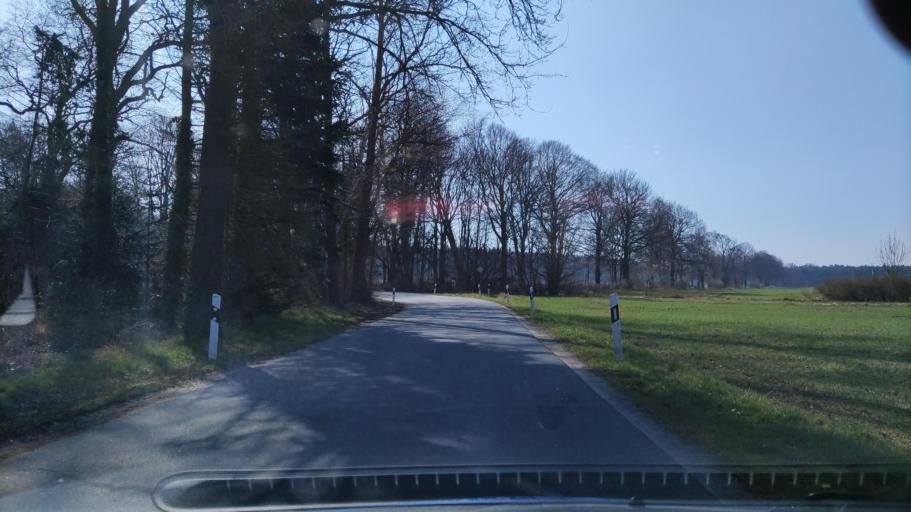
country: DE
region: Lower Saxony
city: Zernien
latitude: 52.9849
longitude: 10.8724
